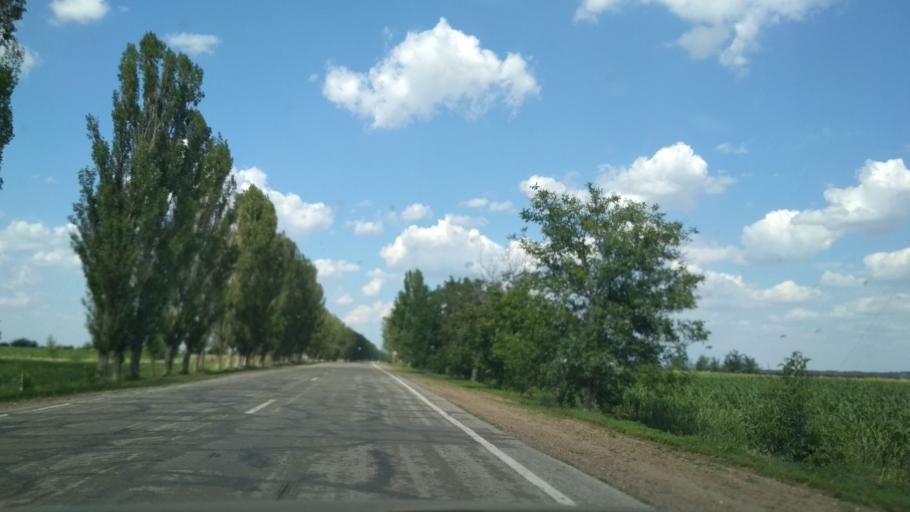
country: MD
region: Chisinau
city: Vadul lui Voda
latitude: 47.1216
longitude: 29.1140
